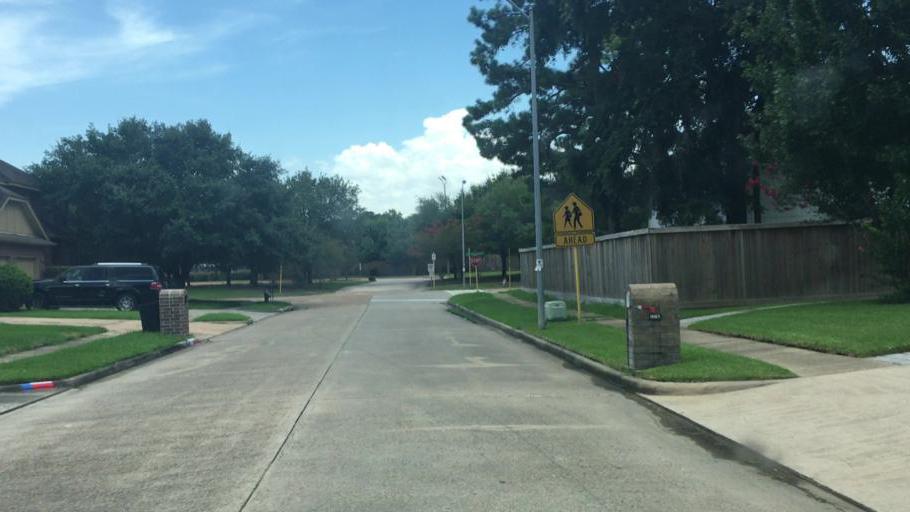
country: US
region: Texas
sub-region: Harris County
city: Atascocita
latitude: 29.9919
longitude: -95.1724
